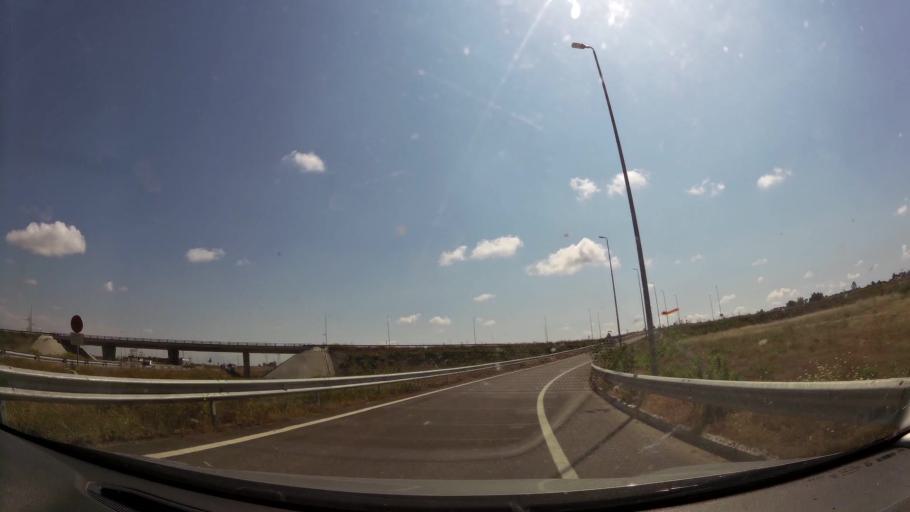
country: MA
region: Rabat-Sale-Zemmour-Zaer
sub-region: Rabat
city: Rabat
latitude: 33.9098
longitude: -6.7769
